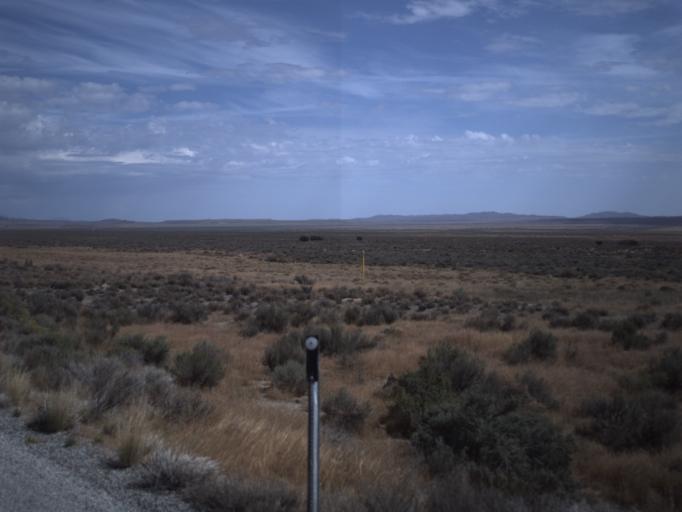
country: US
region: Utah
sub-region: Tooele County
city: Wendover
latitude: 41.5202
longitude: -113.5975
